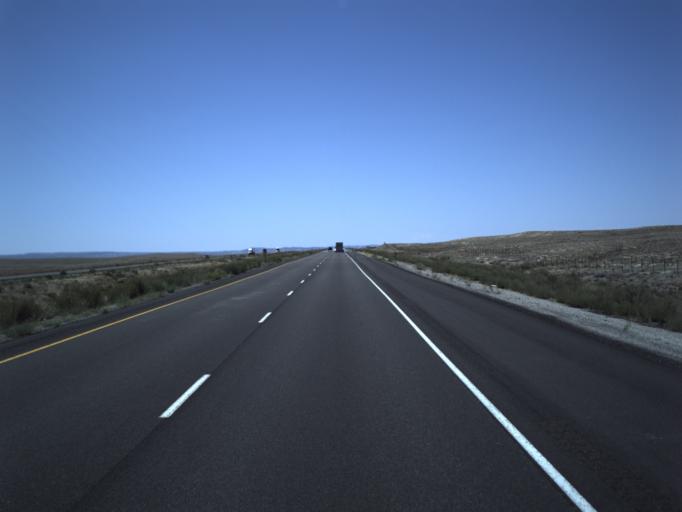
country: US
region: Colorado
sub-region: Mesa County
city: Loma
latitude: 39.0599
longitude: -109.2548
